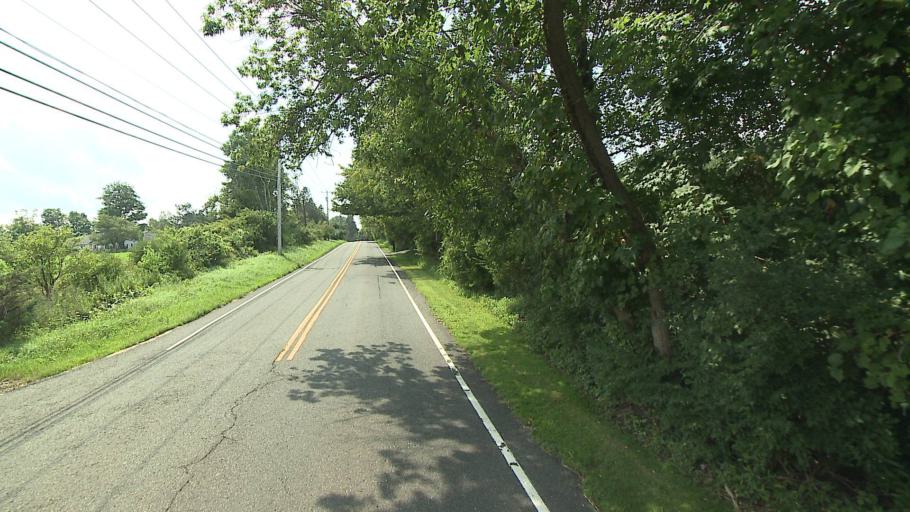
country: US
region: Connecticut
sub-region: Litchfield County
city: New Preston
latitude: 41.6391
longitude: -73.3361
